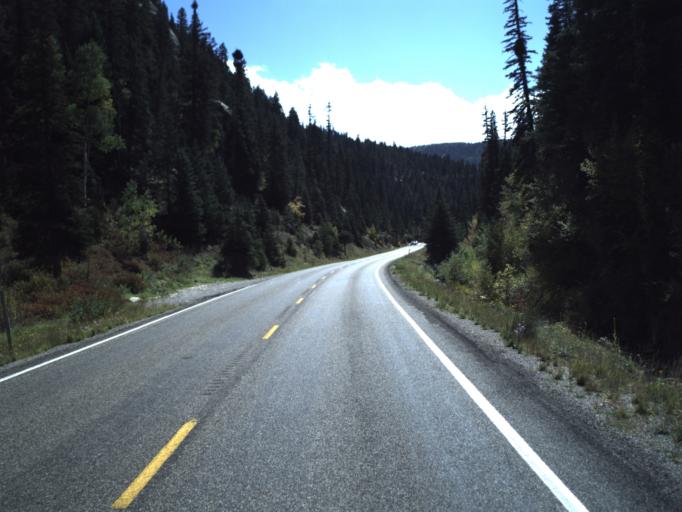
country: US
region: Utah
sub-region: Iron County
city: Cedar City
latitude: 37.6167
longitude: -112.9319
